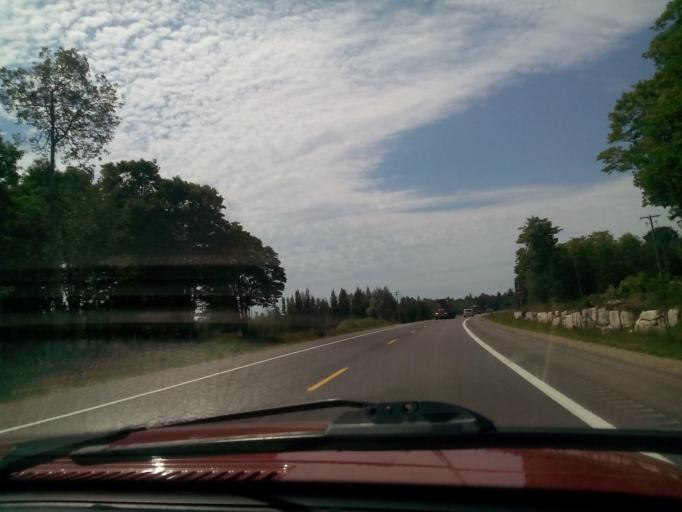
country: US
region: Michigan
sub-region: Schoolcraft County
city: Manistique
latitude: 45.9952
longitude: -86.0075
